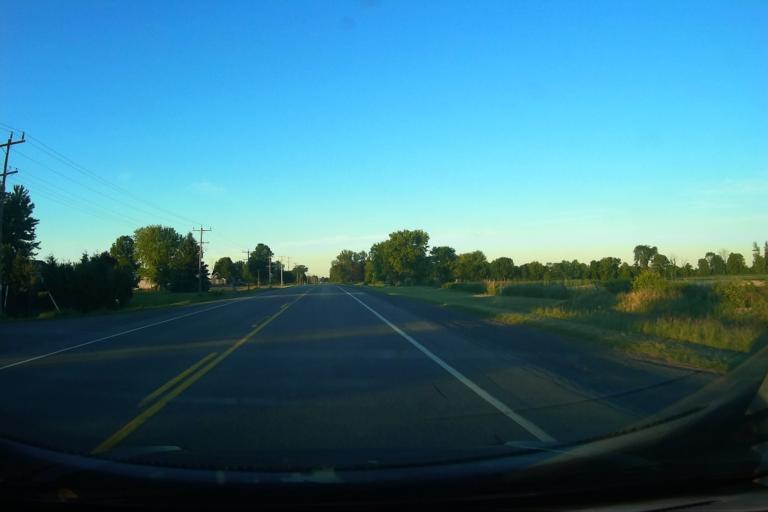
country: CA
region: Ontario
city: Casselman
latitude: 45.0959
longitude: -75.2746
